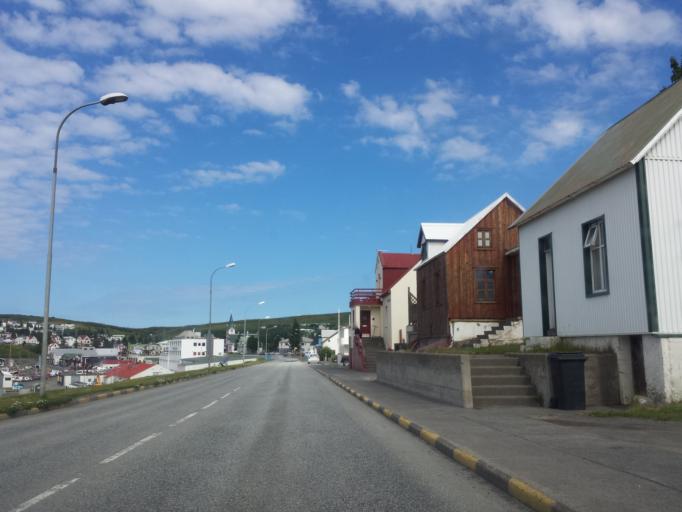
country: IS
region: Northeast
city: Husavik
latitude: 66.0425
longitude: -17.3420
